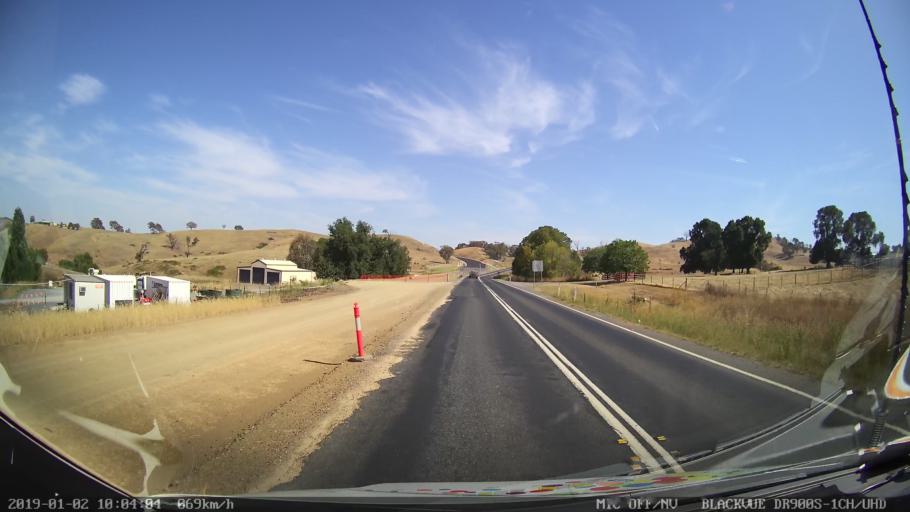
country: AU
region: New South Wales
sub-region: Gundagai
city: Gundagai
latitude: -35.1713
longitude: 148.1241
